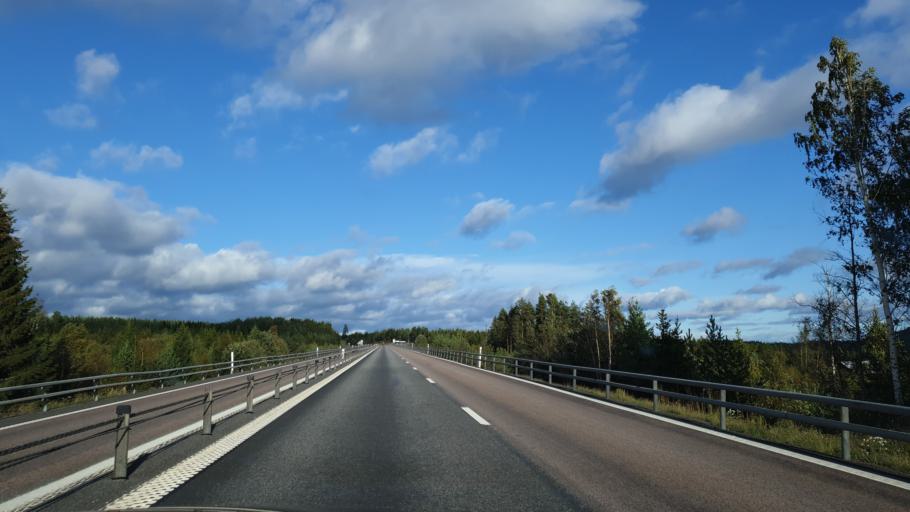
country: SE
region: Vaesternorrland
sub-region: Kramfors Kommun
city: Nordingra
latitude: 62.8770
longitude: 18.0650
